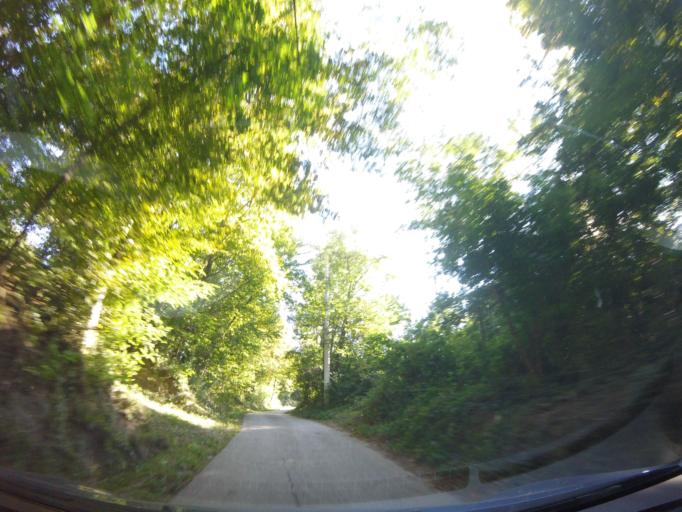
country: HR
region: Zagrebacka
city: Rude
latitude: 45.7586
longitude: 15.6641
